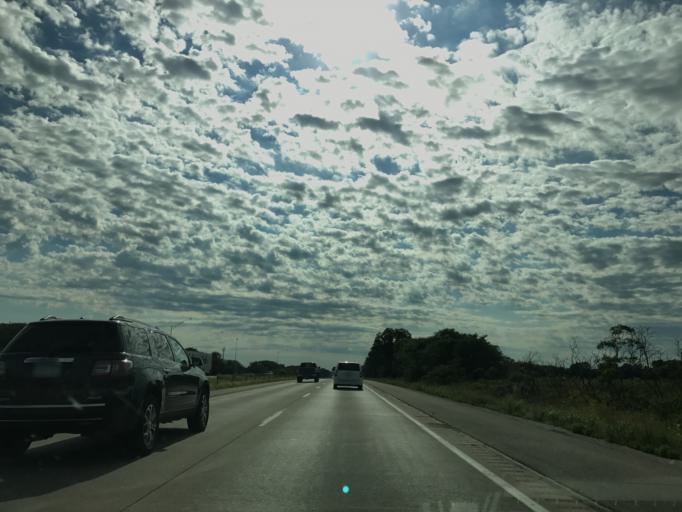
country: US
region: Iowa
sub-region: Dallas County
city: Van Meter
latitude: 41.5545
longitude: -93.9237
